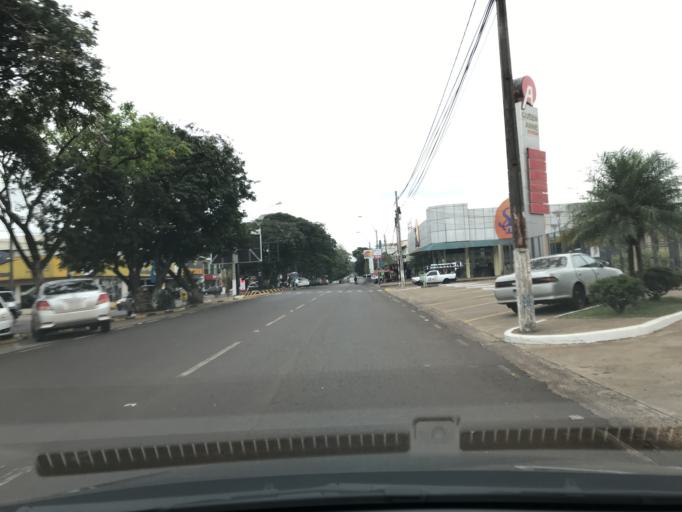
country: PY
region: Canindeyu
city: Salto del Guaira
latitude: -24.0618
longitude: -54.3072
